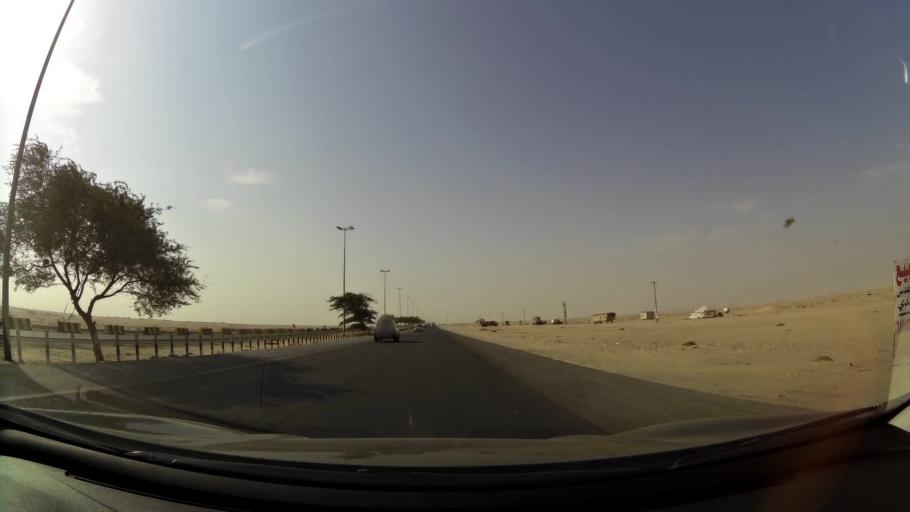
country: KW
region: Al Ahmadi
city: Al Ahmadi
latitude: 28.9204
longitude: 48.1014
